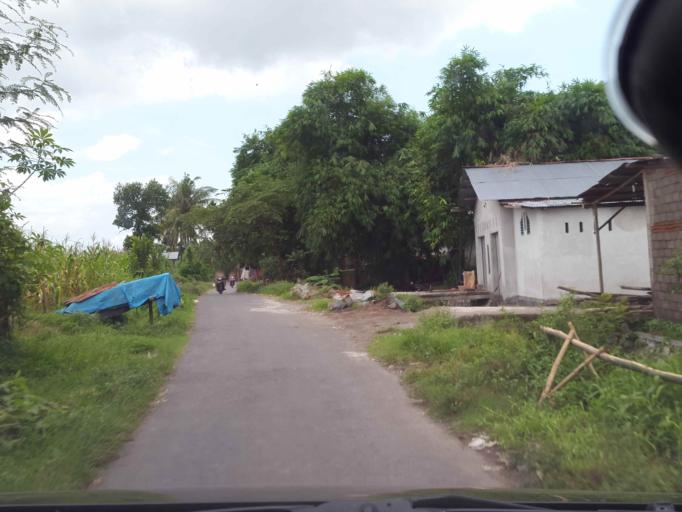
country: ID
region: West Nusa Tenggara
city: Kediri
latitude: -8.6453
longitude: 116.1422
